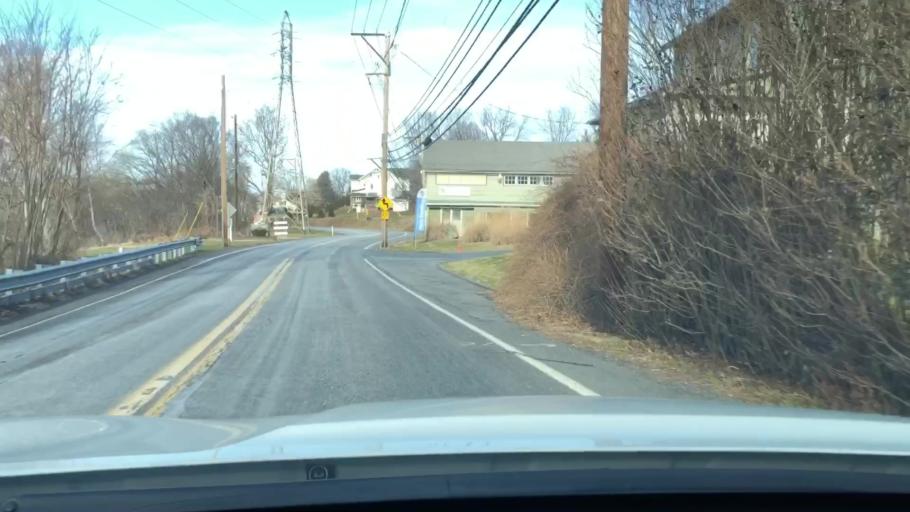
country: US
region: Pennsylvania
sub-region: Lehigh County
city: Catasauqua
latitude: 40.6440
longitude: -75.4633
